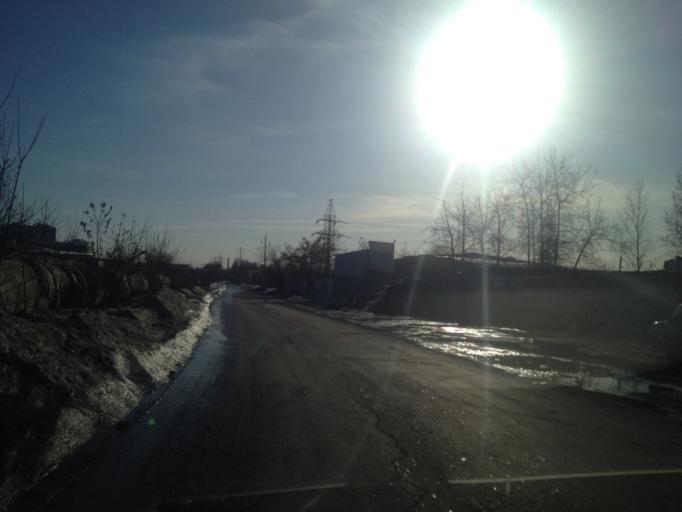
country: RU
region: Sverdlovsk
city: Yekaterinburg
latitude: 56.8792
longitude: 60.5489
